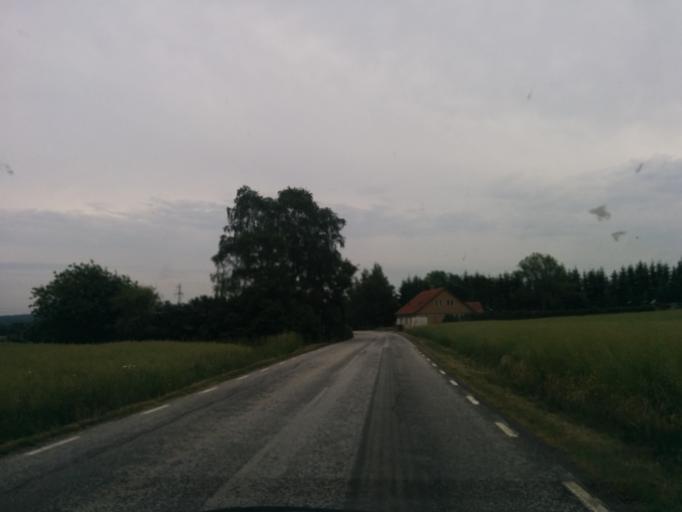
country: SE
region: Skane
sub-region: Lunds Kommun
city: Genarp
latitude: 55.6372
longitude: 13.3668
